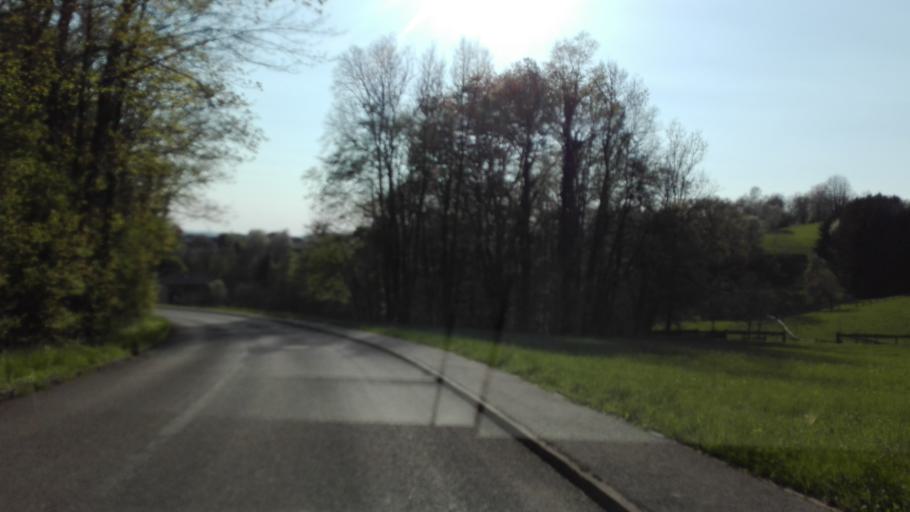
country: AT
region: Upper Austria
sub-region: Politischer Bezirk Grieskirchen
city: Grieskirchen
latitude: 48.3510
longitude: 13.7767
